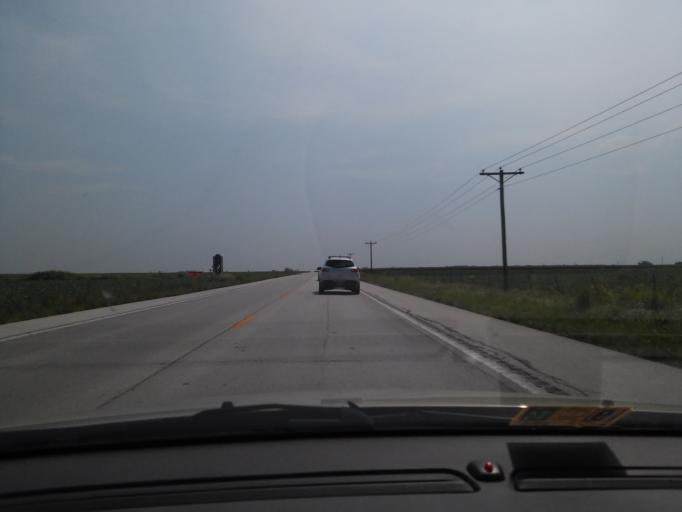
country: US
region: Missouri
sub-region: Audrain County
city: Mexico
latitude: 39.1639
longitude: -91.7370
